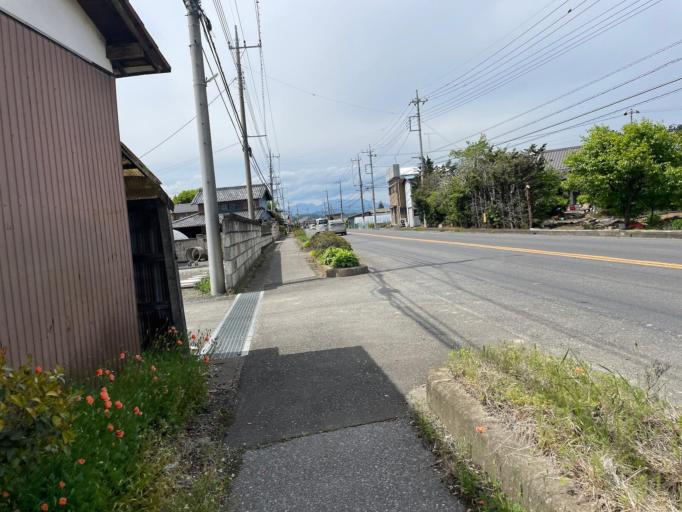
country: JP
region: Tochigi
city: Mibu
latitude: 36.4666
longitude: 139.7665
